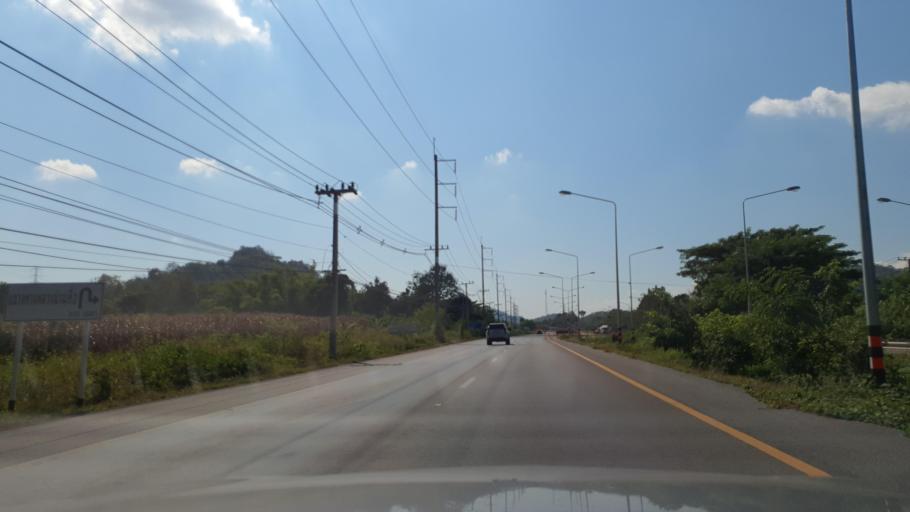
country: TH
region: Nan
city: Nan
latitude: 18.8931
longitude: 100.7541
